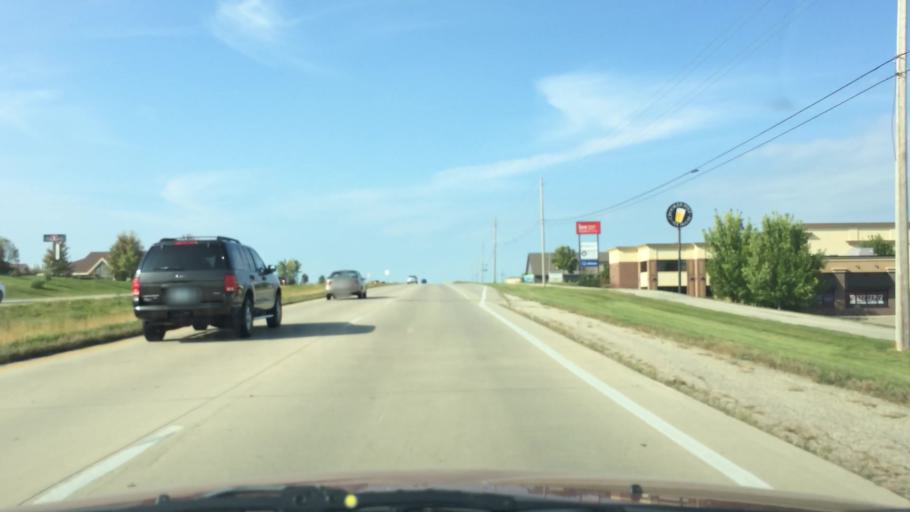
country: US
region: Minnesota
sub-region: Olmsted County
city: Rochester
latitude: 44.0518
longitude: -92.5224
